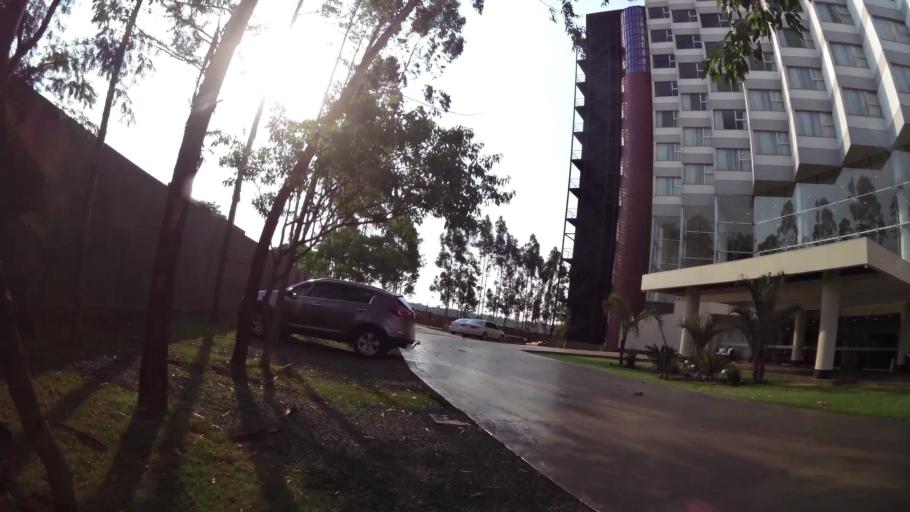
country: PY
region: Alto Parana
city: Ciudad del Este
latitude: -25.4959
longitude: -54.6651
